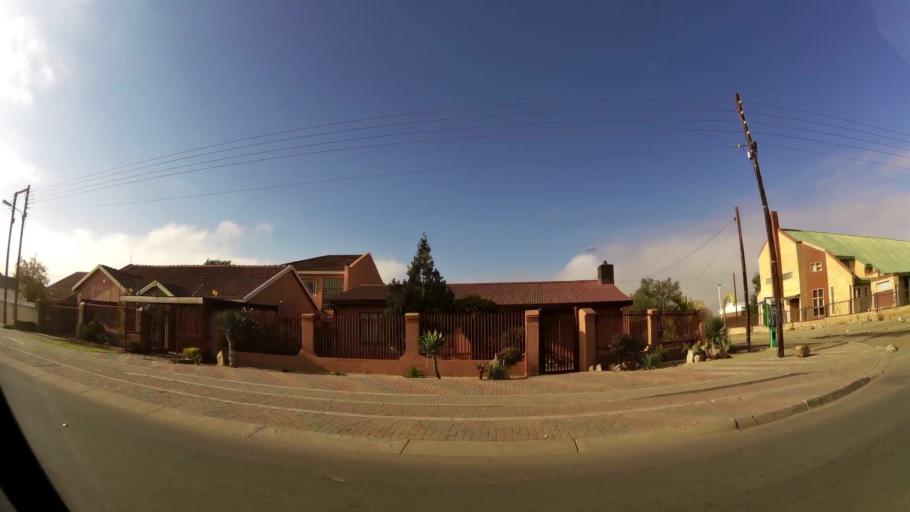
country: ZA
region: Limpopo
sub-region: Capricorn District Municipality
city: Polokwane
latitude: -23.8465
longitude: 29.3860
